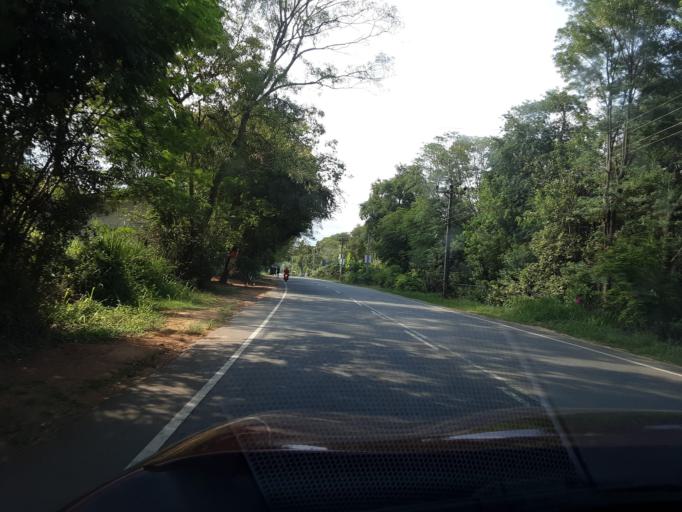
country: LK
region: Uva
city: Haputale
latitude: 6.6099
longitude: 81.1338
